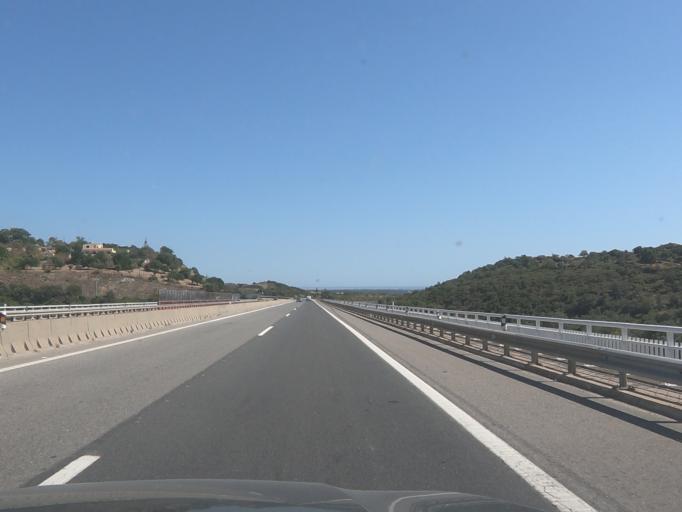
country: PT
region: Faro
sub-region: Loule
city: Almancil
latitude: 37.1051
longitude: -8.0159
